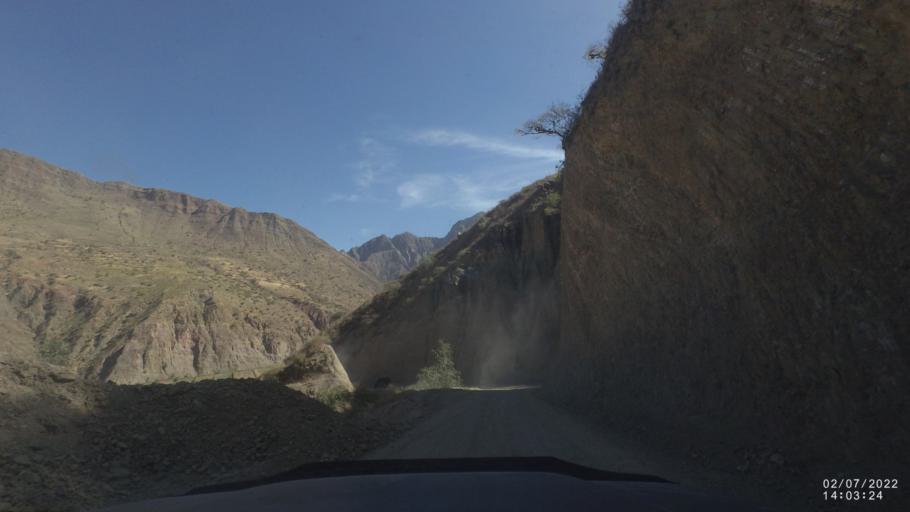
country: BO
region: Cochabamba
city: Irpa Irpa
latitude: -17.8229
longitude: -66.3905
